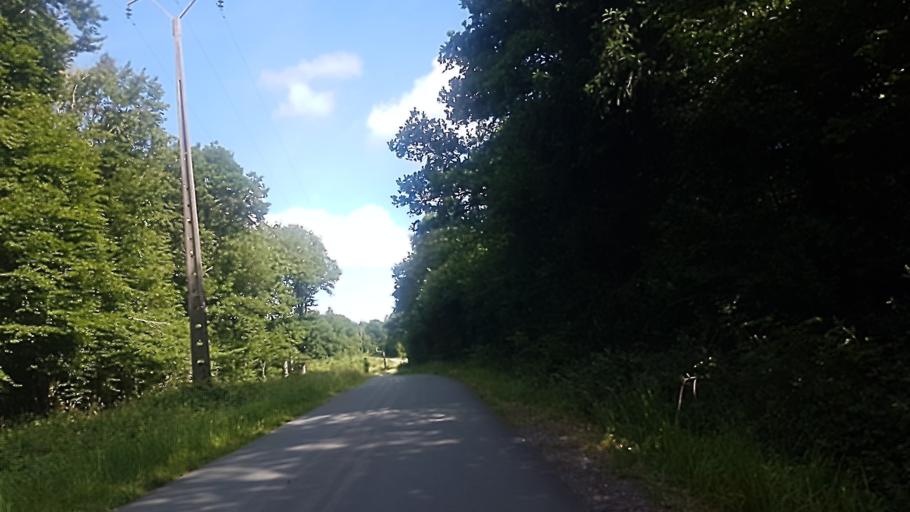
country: BE
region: Wallonia
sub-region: Province de Namur
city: Couvin
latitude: 50.0459
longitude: 4.5621
